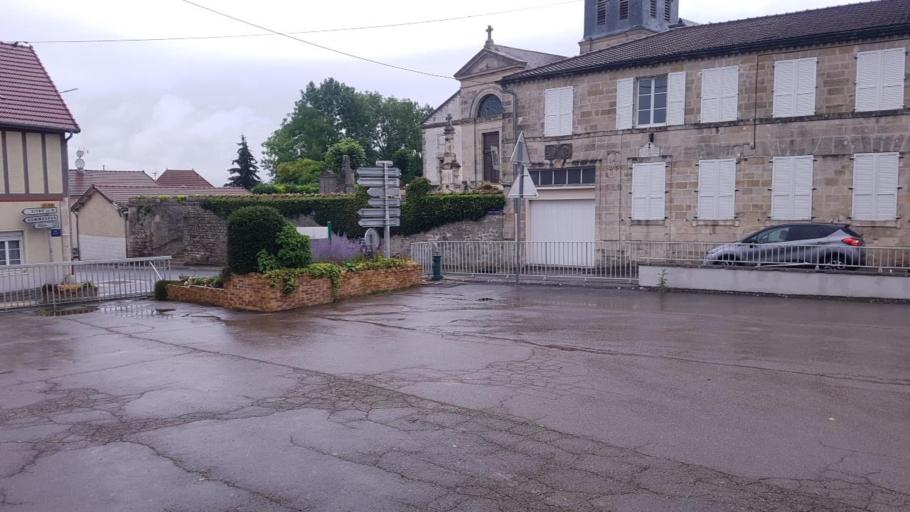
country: FR
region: Champagne-Ardenne
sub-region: Departement de la Marne
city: Sarry
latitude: 48.8574
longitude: 4.4834
